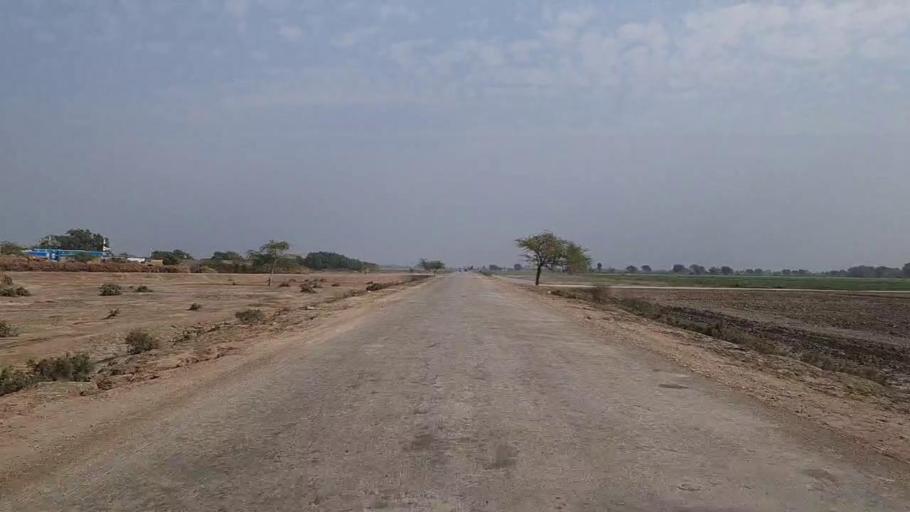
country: PK
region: Sindh
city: Mirwah Gorchani
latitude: 25.4117
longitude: 69.0383
